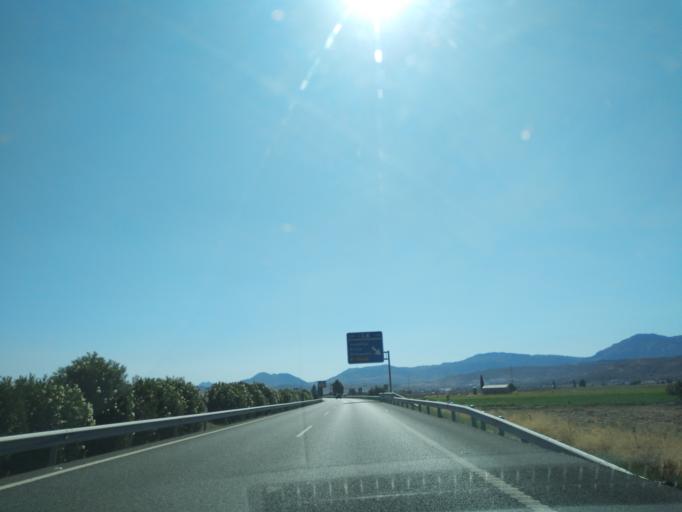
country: ES
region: Andalusia
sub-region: Provincia de Malaga
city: Mollina
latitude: 37.0775
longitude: -4.6106
